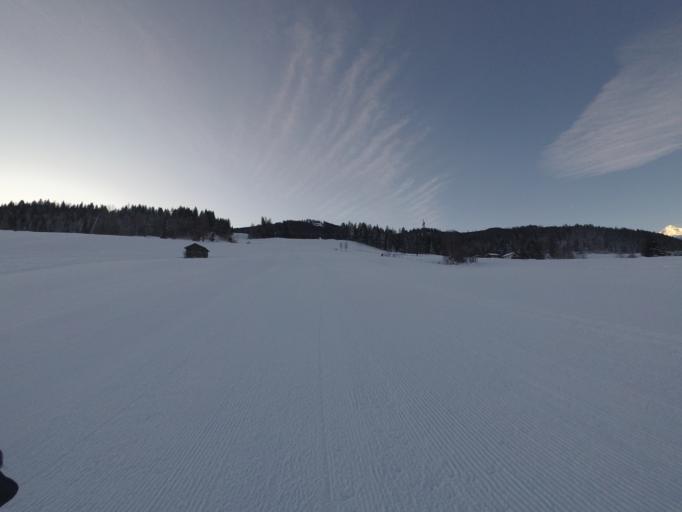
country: AT
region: Salzburg
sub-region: Politischer Bezirk Zell am See
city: Taxenbach
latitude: 47.2881
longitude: 13.0030
